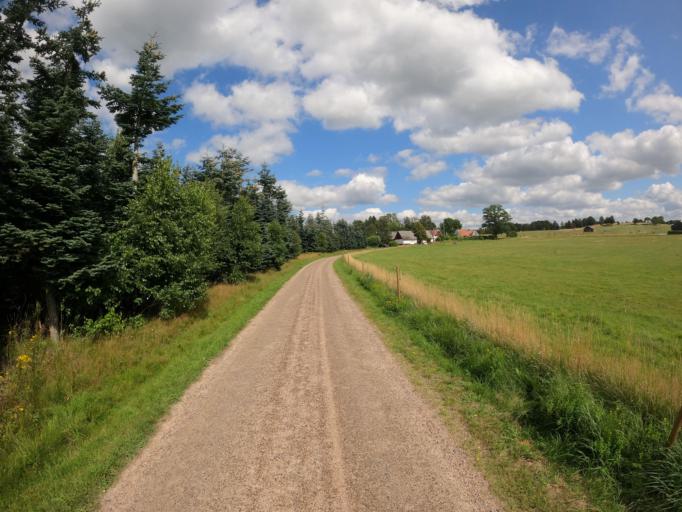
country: SE
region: Skane
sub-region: Lunds Kommun
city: Veberod
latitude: 55.6007
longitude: 13.4869
